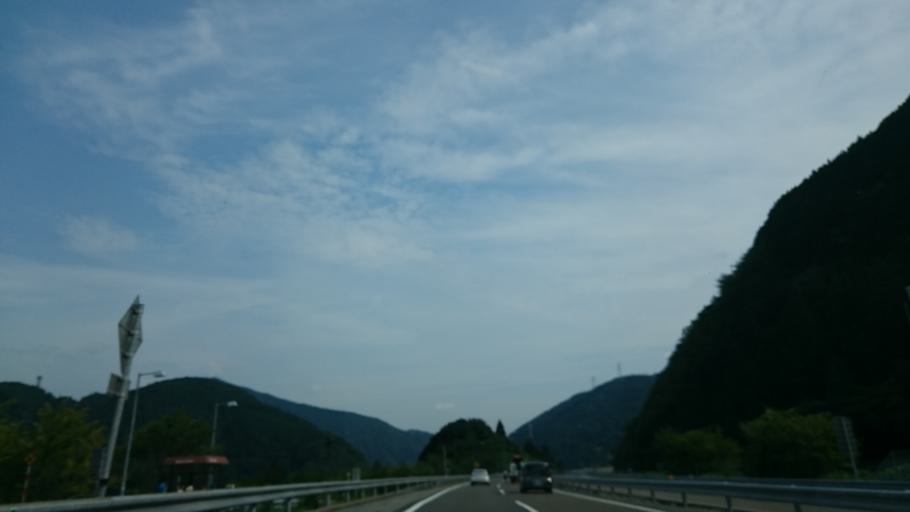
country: JP
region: Gifu
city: Gujo
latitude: 35.7485
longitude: 136.9446
